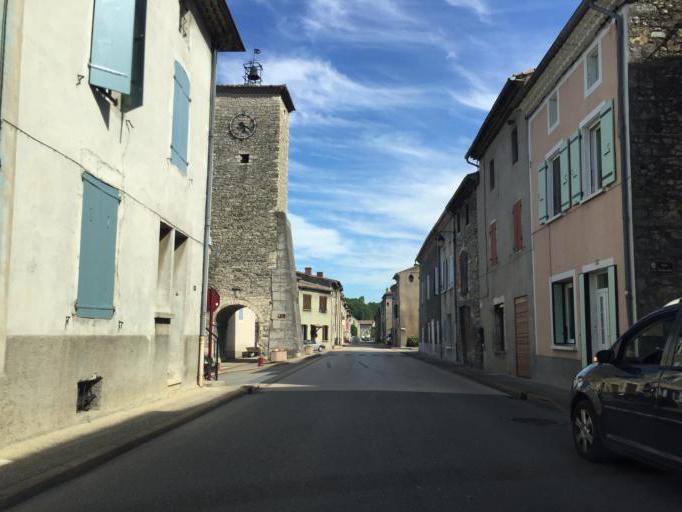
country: FR
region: Rhone-Alpes
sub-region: Departement de la Drome
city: Saulce-sur-Rhone
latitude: 44.7124
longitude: 4.7636
